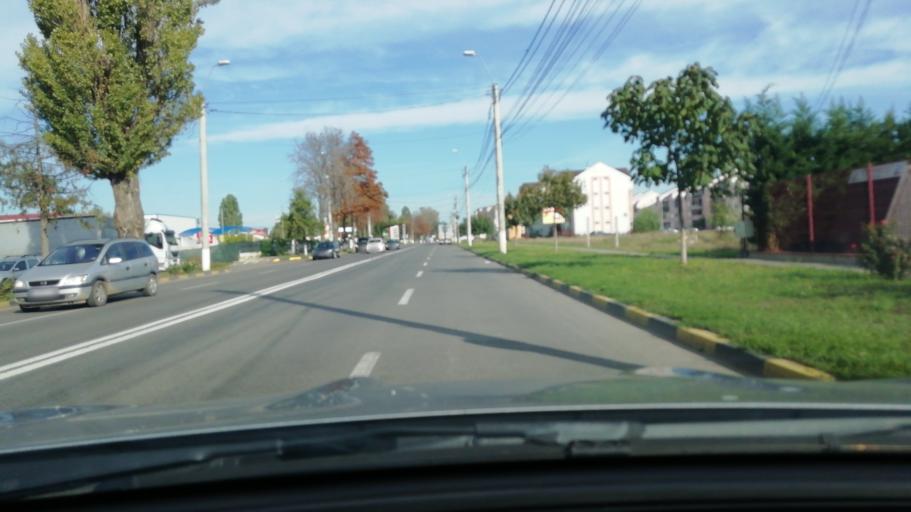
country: RO
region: Galati
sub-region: Municipiul Tecuci
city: Tecuci
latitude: 45.8242
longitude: 27.4382
